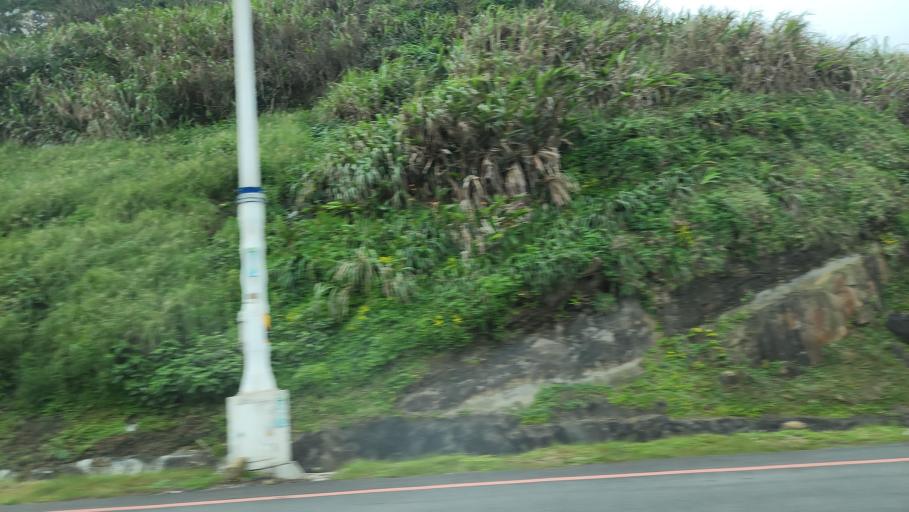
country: TW
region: Taiwan
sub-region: Keelung
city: Keelung
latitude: 25.1647
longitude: 121.7170
